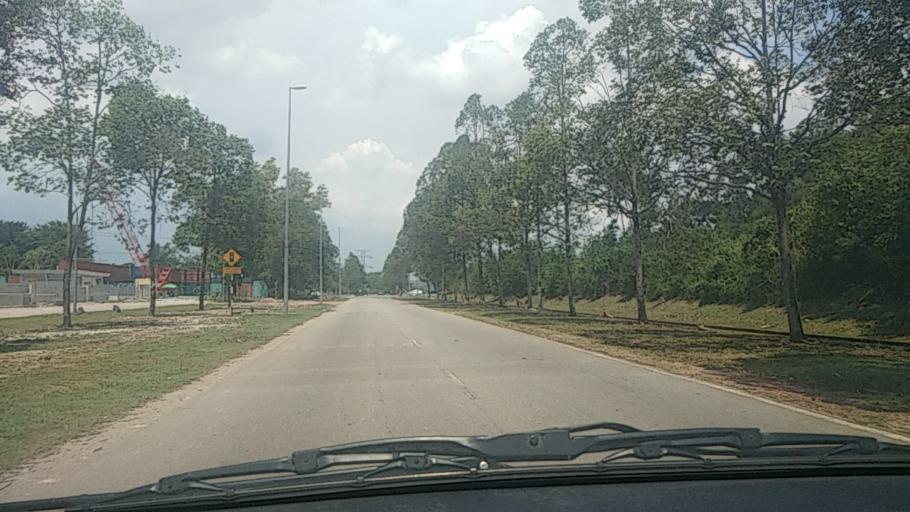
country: MY
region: Kedah
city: Sungai Petani
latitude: 5.6477
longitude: 100.5313
